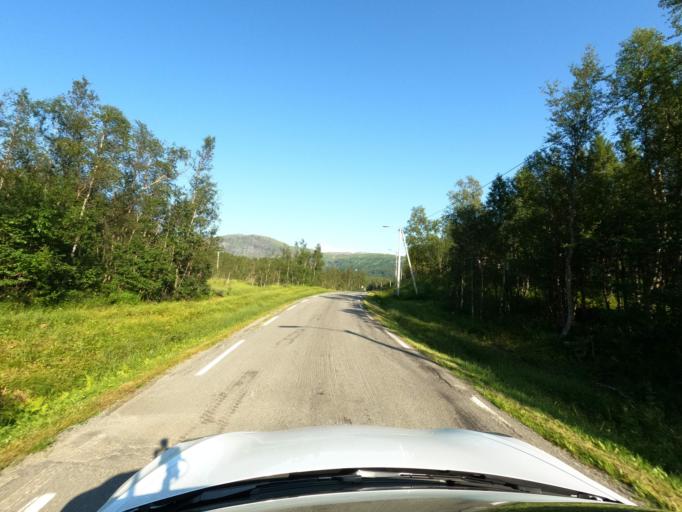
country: NO
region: Troms
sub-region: Gratangen
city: Gratangen
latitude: 68.5609
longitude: 17.7071
